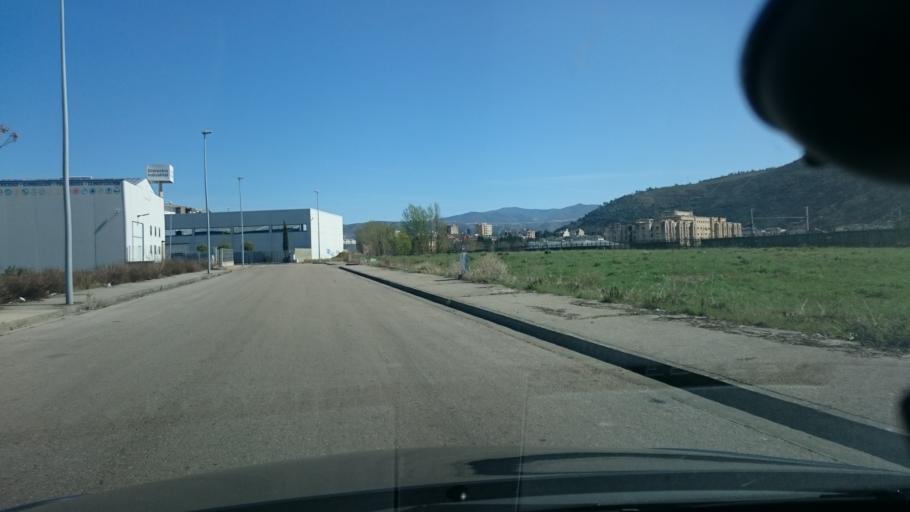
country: ES
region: Castille and Leon
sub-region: Provincia de Leon
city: Ponferrada
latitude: 42.5515
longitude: -6.6156
